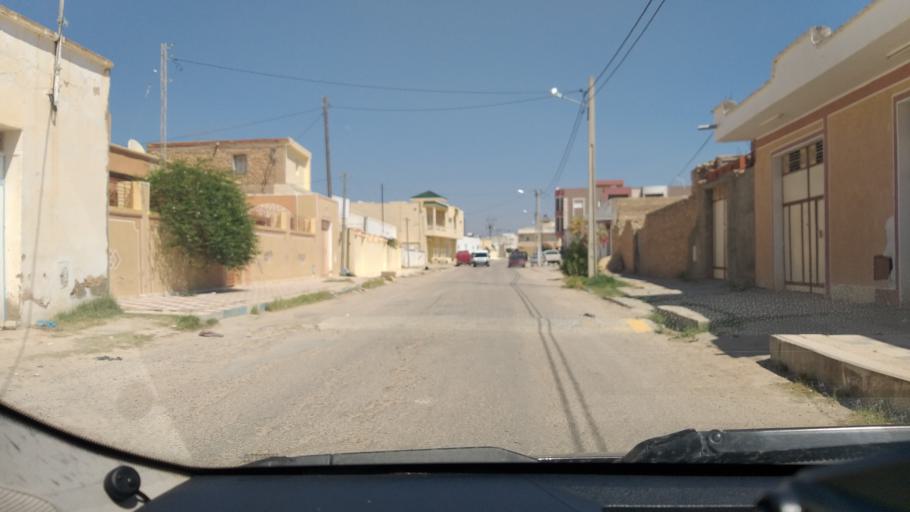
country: TN
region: Al Mahdiyah
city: El Jem
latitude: 35.2927
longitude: 10.7131
